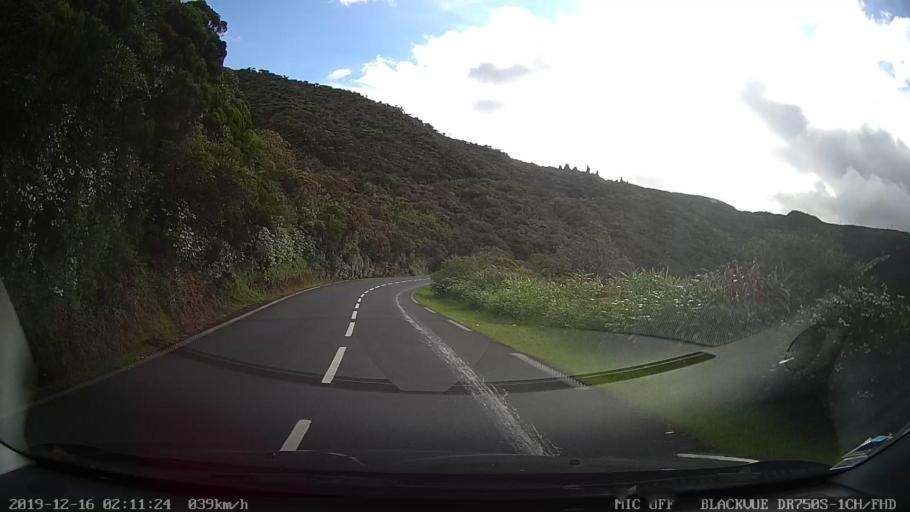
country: RE
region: Reunion
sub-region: Reunion
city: Cilaos
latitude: -21.1619
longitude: 55.5961
